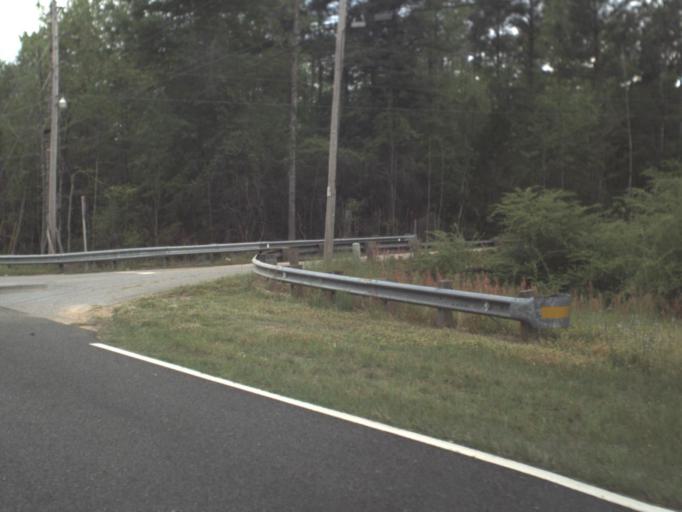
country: US
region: Florida
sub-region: Escambia County
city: Molino
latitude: 30.8426
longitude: -87.3248
